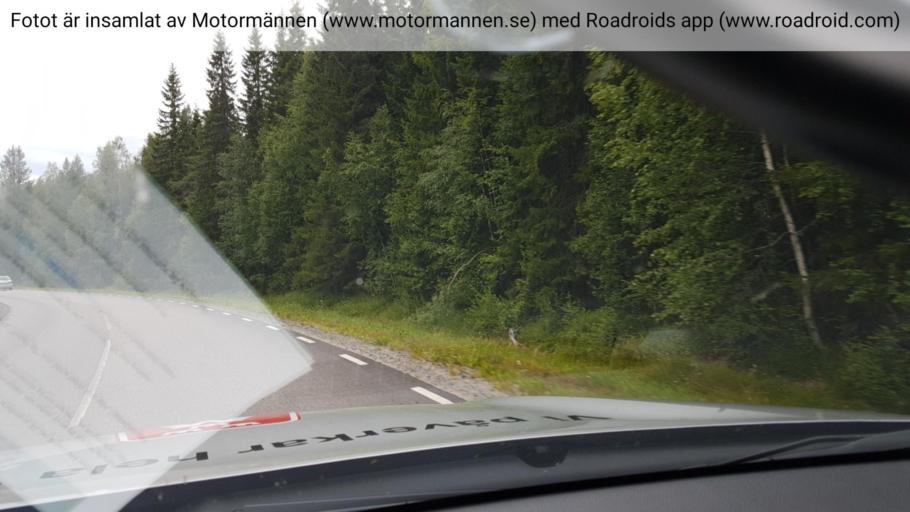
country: SE
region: Norrbotten
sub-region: Lulea Kommun
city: Gammelstad
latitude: 65.6565
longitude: 22.0395
